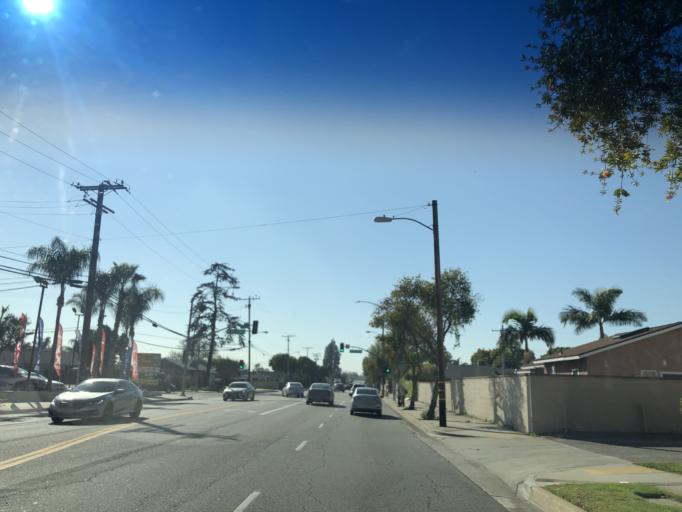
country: US
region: California
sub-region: Los Angeles County
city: South Whittier
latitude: 33.9421
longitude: -118.0293
